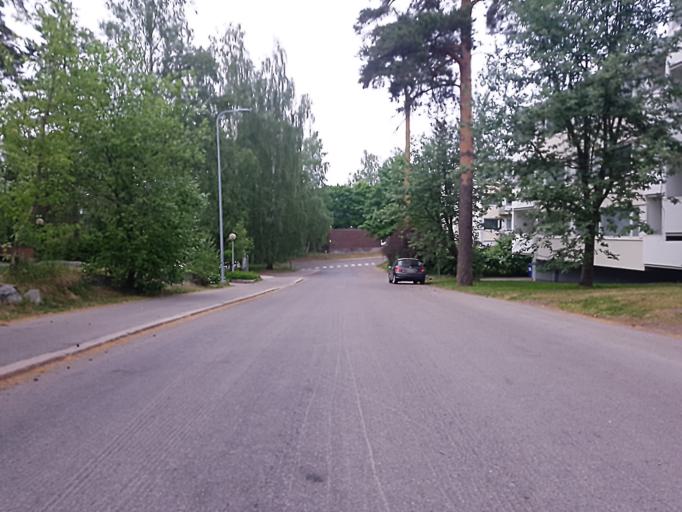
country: FI
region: Uusimaa
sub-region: Helsinki
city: Helsinki
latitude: 60.2241
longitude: 24.9704
